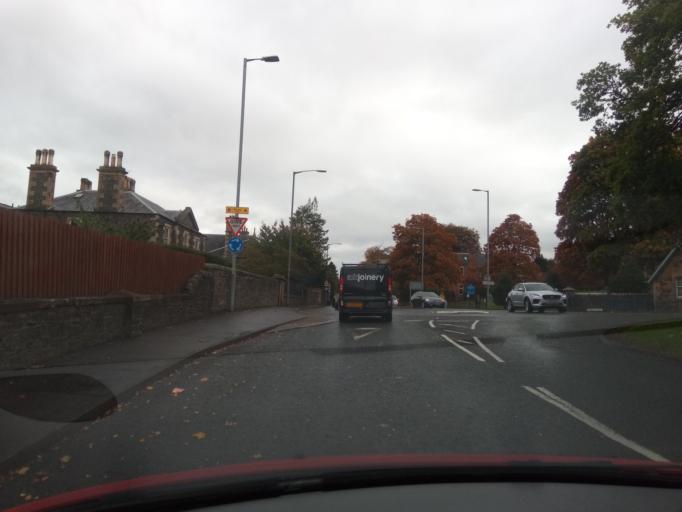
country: GB
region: Scotland
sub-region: The Scottish Borders
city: Galashiels
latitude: 55.6120
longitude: -2.8027
